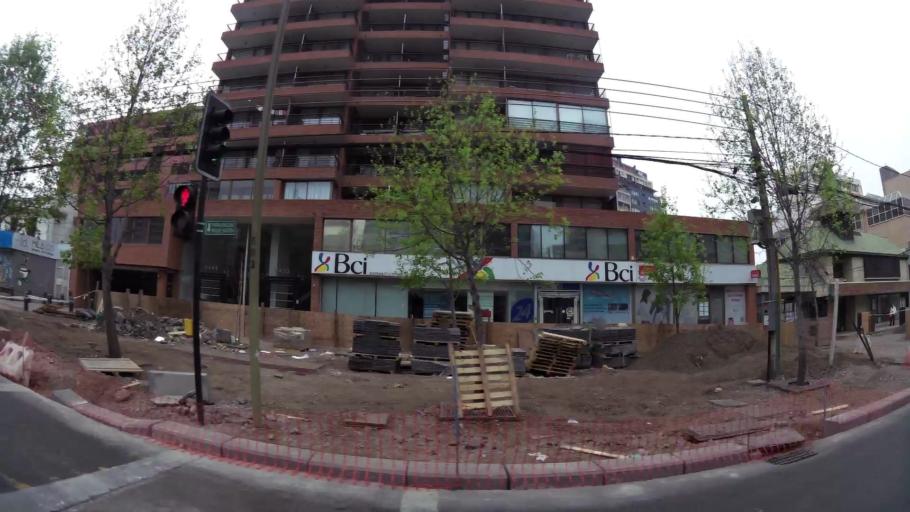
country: CL
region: Santiago Metropolitan
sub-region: Provincia de Santiago
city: Villa Presidente Frei, Nunoa, Santiago, Chile
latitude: -33.4081
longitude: -70.5640
